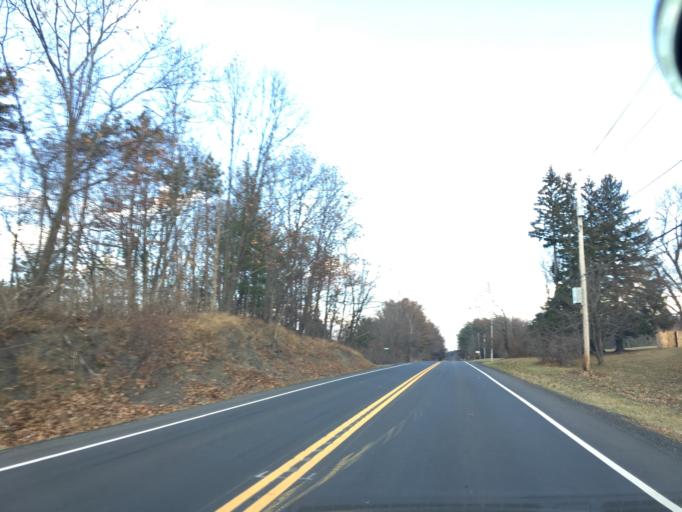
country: US
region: New York
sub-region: Rensselaer County
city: West Sand Lake
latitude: 42.6129
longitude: -73.6050
